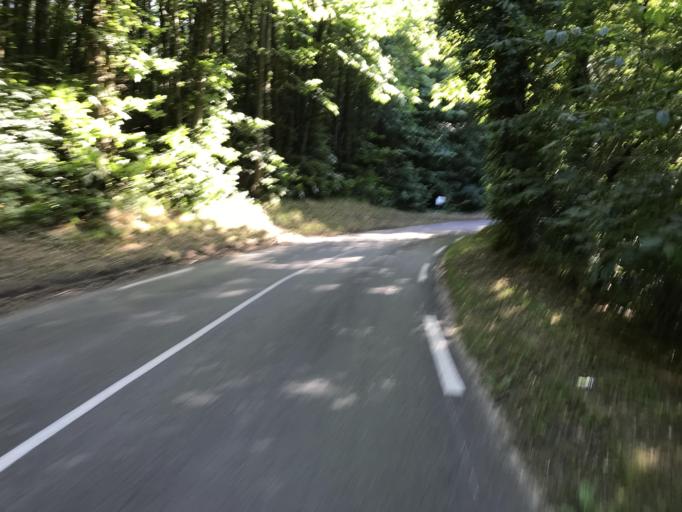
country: FR
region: Ile-de-France
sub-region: Departement de l'Essonne
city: Villejust
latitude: 48.6834
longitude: 2.2471
